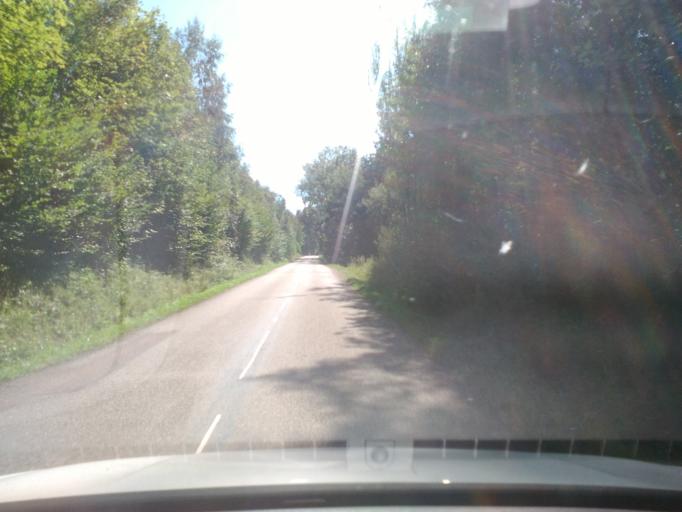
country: FR
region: Lorraine
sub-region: Departement des Vosges
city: Senones
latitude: 48.3835
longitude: 6.9621
